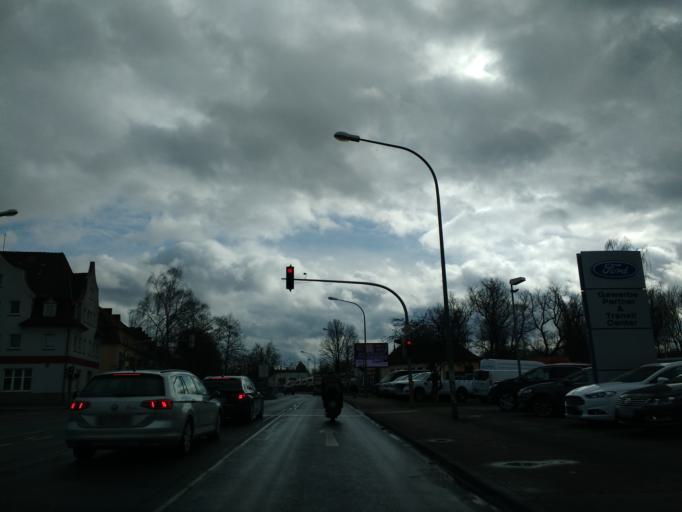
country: DE
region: Lower Saxony
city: Osnabrueck
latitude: 52.2864
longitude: 8.0388
